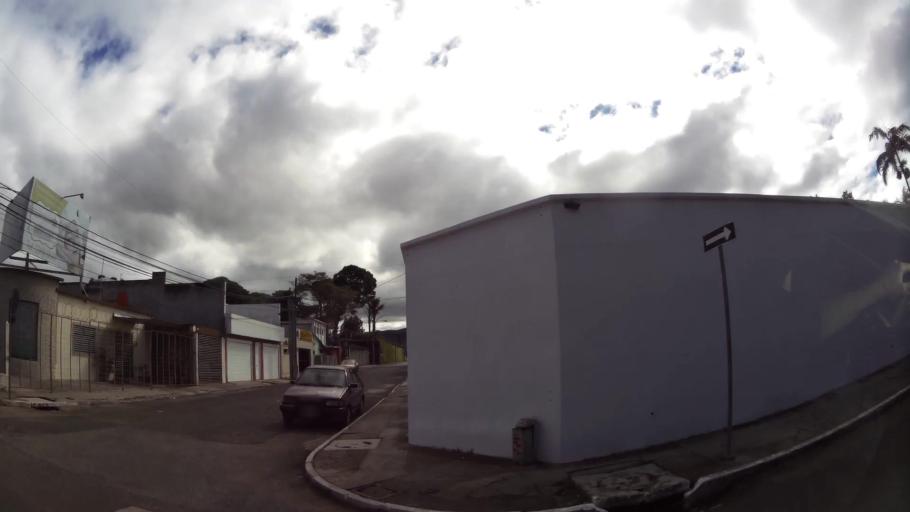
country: GT
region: Guatemala
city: Santa Catarina Pinula
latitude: 14.5943
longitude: -90.5070
